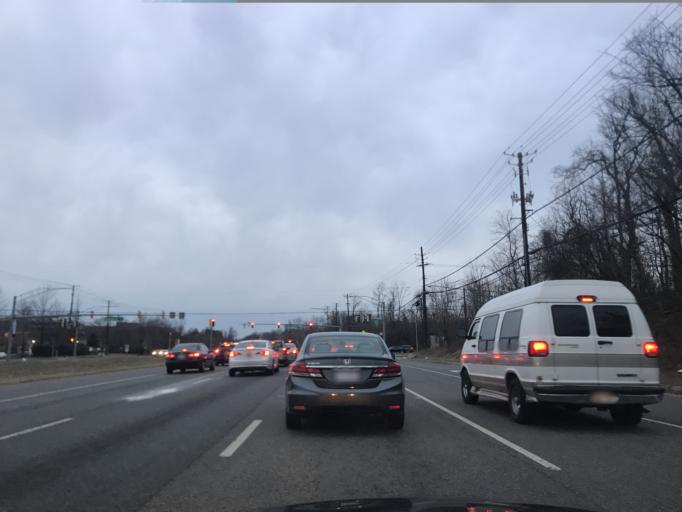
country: US
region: Maryland
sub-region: Prince George's County
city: Lake Arbor
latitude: 38.9122
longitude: -76.8376
